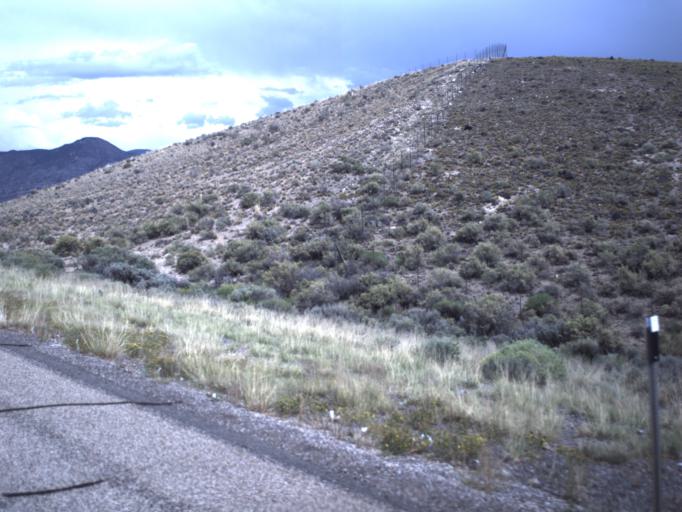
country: US
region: Utah
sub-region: Piute County
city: Junction
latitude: 38.2035
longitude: -112.2311
